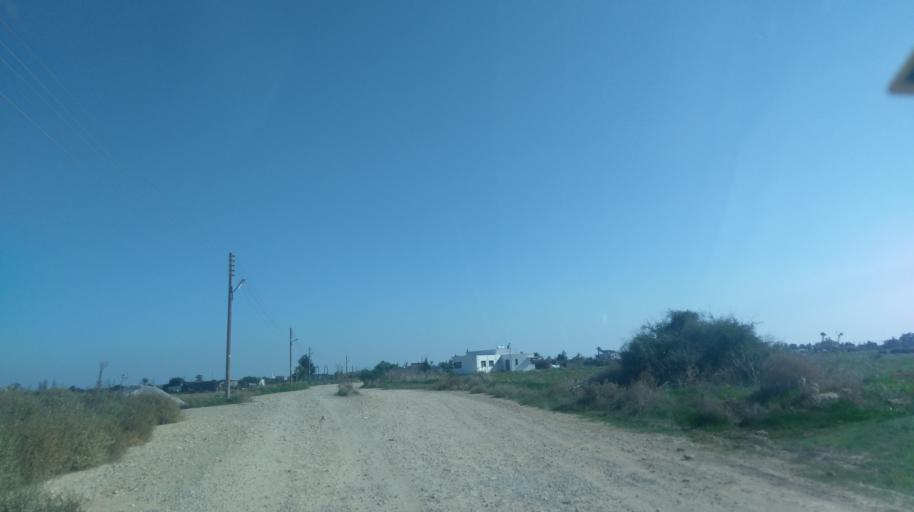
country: CY
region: Ammochostos
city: Trikomo
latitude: 35.2398
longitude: 33.8517
